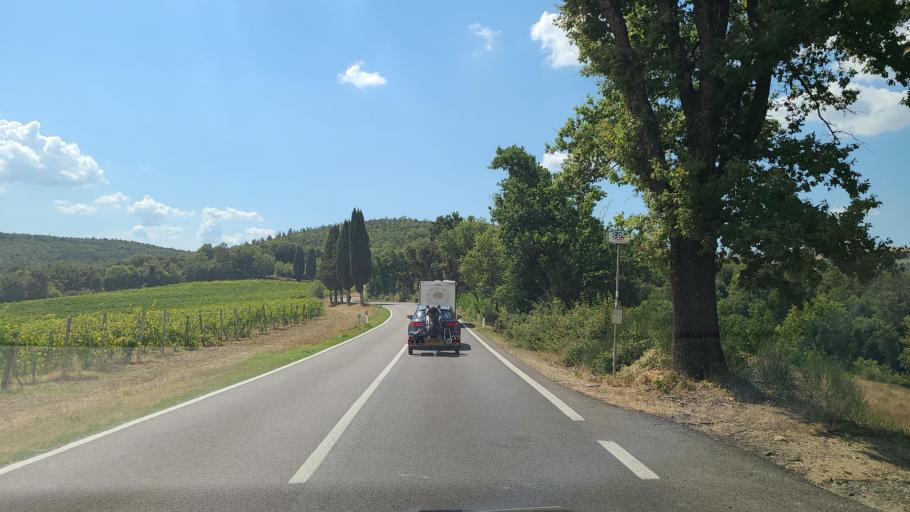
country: IT
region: Tuscany
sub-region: Provincia di Siena
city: San Gimignano
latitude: 43.4035
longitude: 11.0066
